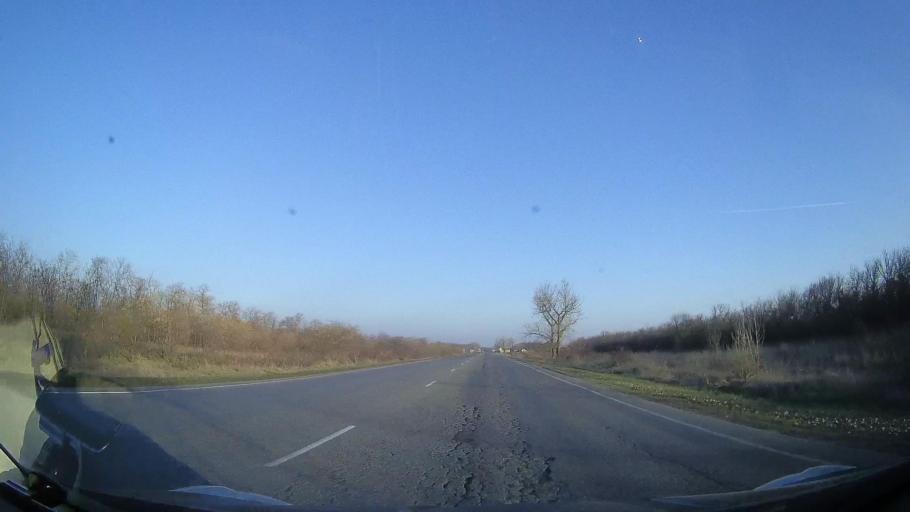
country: RU
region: Rostov
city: Kirovskaya
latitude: 47.0152
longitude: 39.9156
